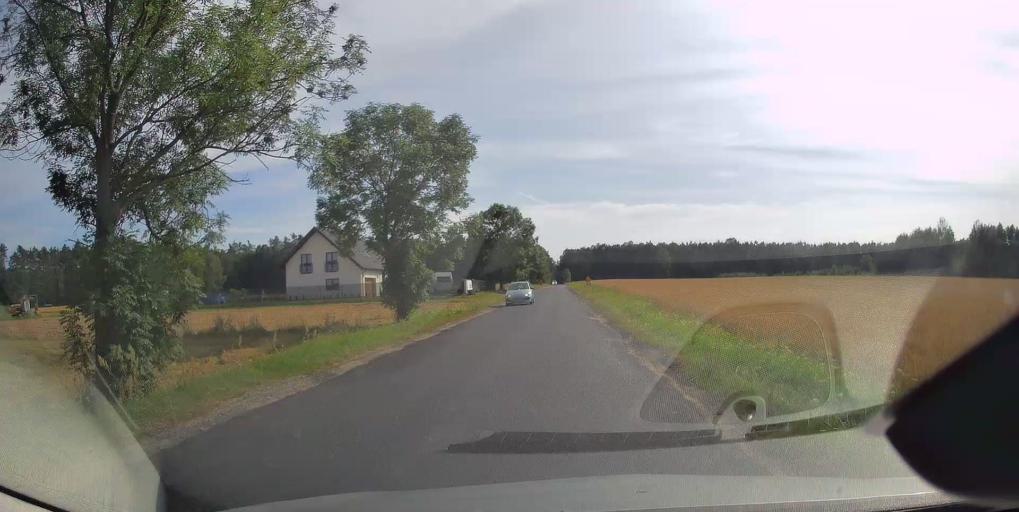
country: PL
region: Lodz Voivodeship
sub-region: Powiat opoczynski
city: Mniszkow
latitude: 51.4442
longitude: 20.0276
